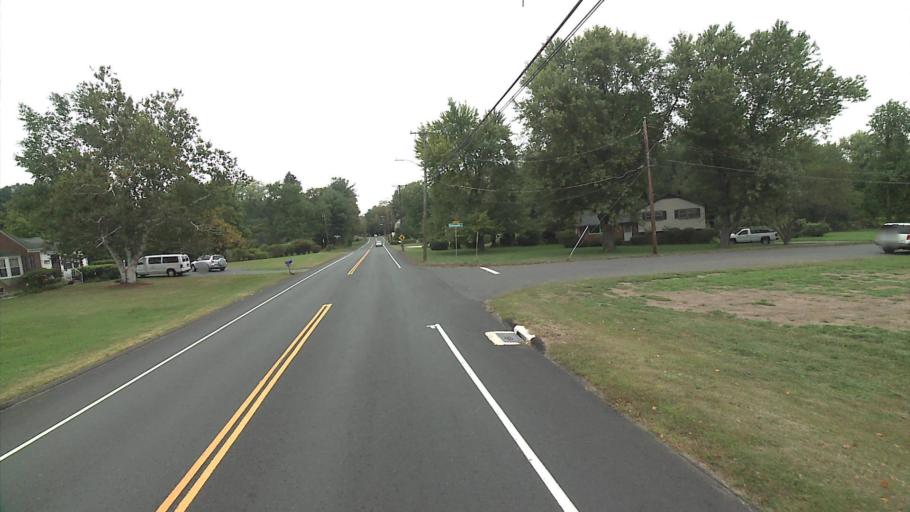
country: US
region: Connecticut
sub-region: Hartford County
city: Windsor
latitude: 41.8852
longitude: -72.6690
